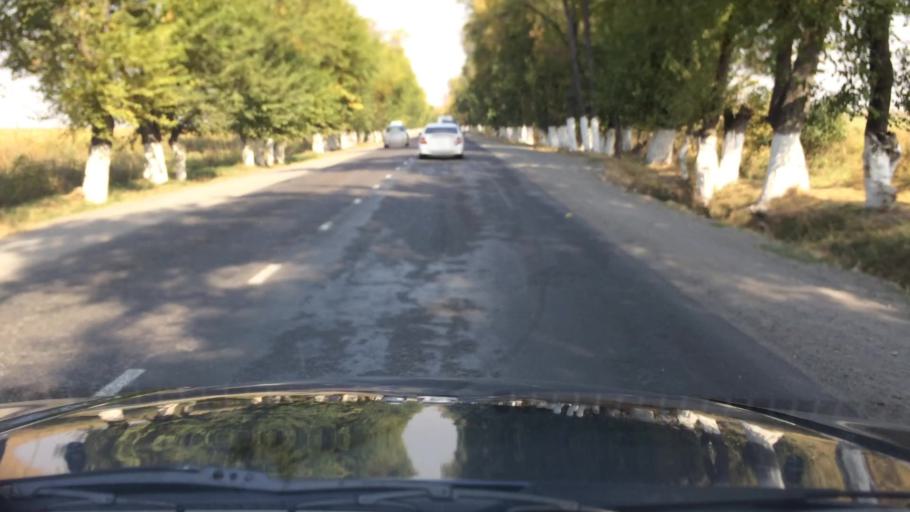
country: KG
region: Chuy
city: Lebedinovka
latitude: 42.9059
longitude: 74.6864
